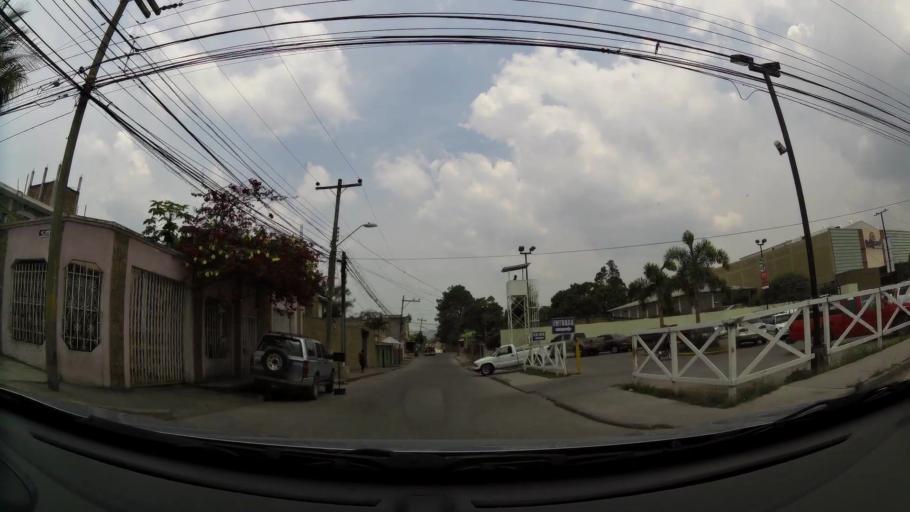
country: HN
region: Comayagua
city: Siguatepeque
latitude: 14.5936
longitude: -87.8310
